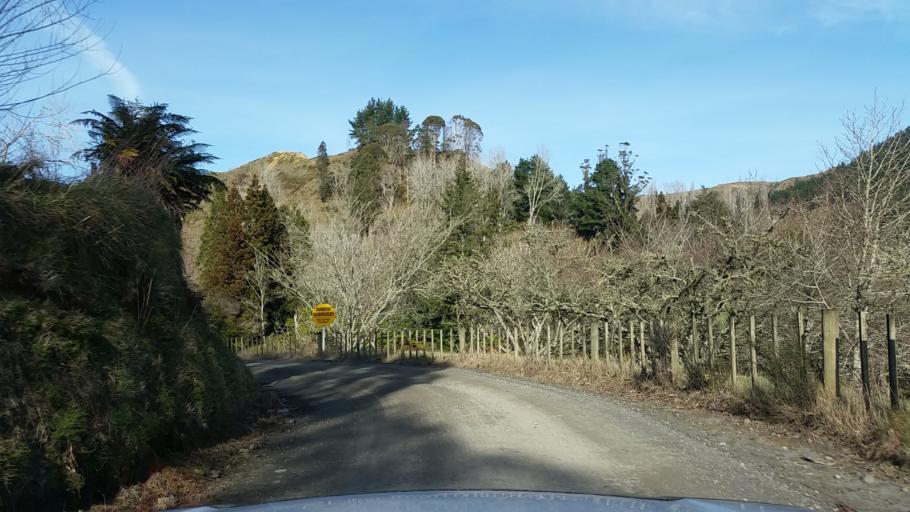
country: NZ
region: Taranaki
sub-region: South Taranaki District
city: Eltham
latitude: -39.3573
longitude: 174.5119
